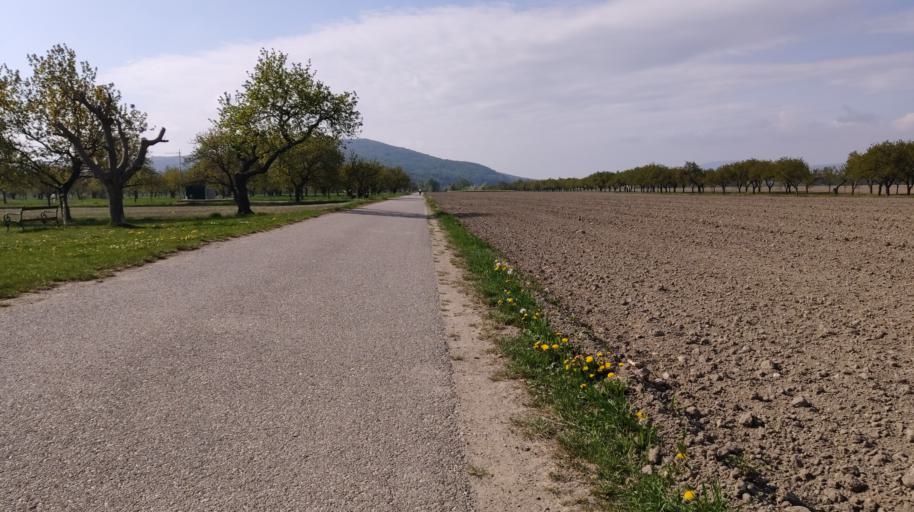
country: AT
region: Burgenland
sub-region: Politischer Bezirk Neusiedl am See
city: Kittsee
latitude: 48.1006
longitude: 17.0560
